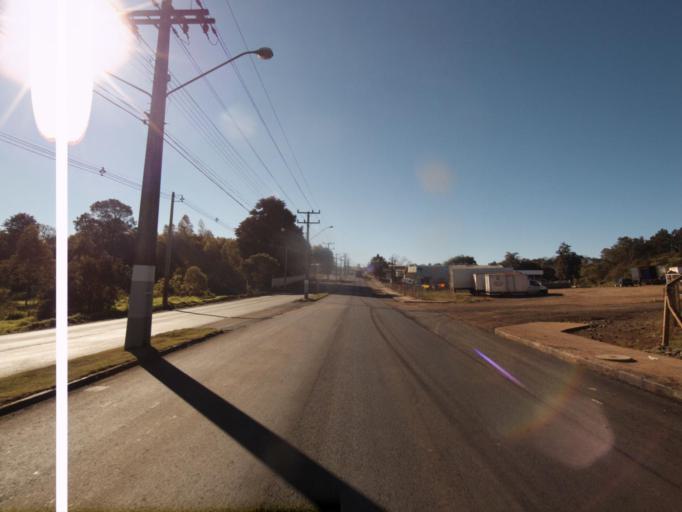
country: AR
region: Misiones
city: Bernardo de Irigoyen
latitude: -26.7419
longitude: -53.5011
